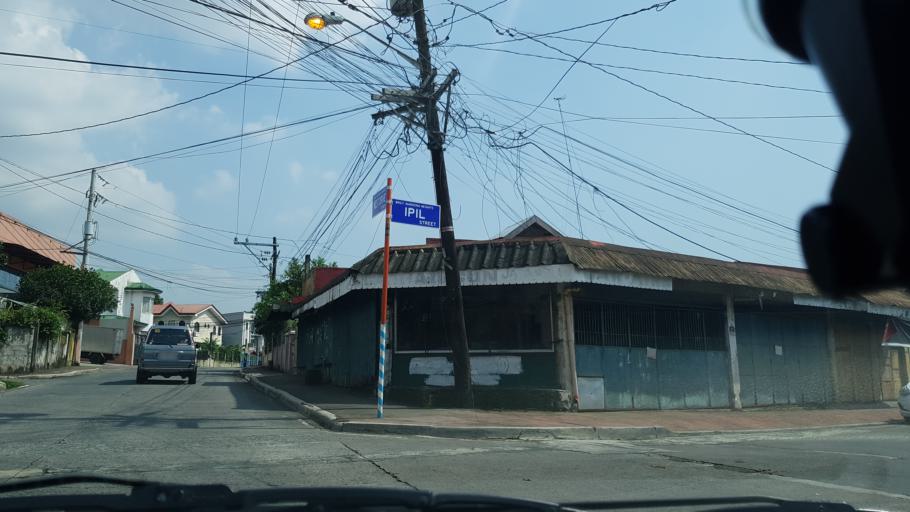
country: PH
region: Calabarzon
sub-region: Province of Rizal
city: Antipolo
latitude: 14.6556
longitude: 121.1155
